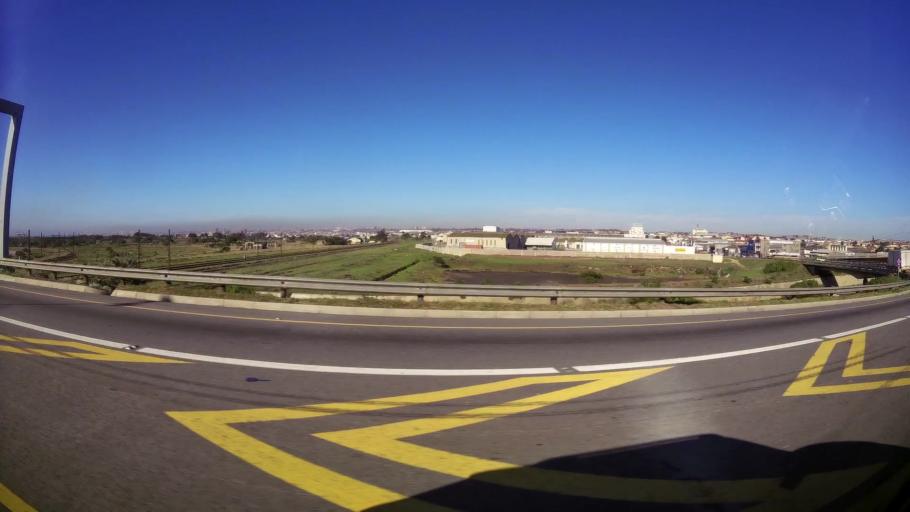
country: ZA
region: Eastern Cape
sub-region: Nelson Mandela Bay Metropolitan Municipality
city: Port Elizabeth
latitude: -33.9138
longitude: 25.6044
